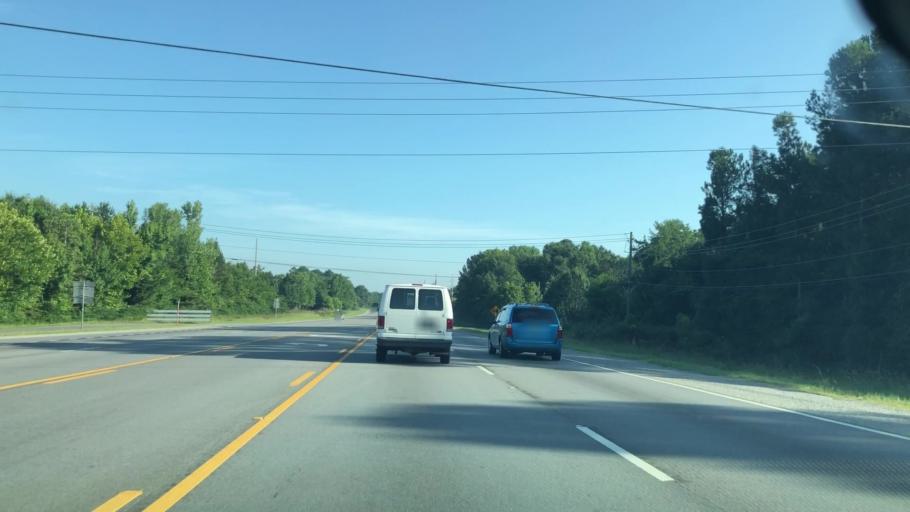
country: US
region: Alabama
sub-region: Calhoun County
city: Bynum
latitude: 33.5975
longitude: -85.9254
